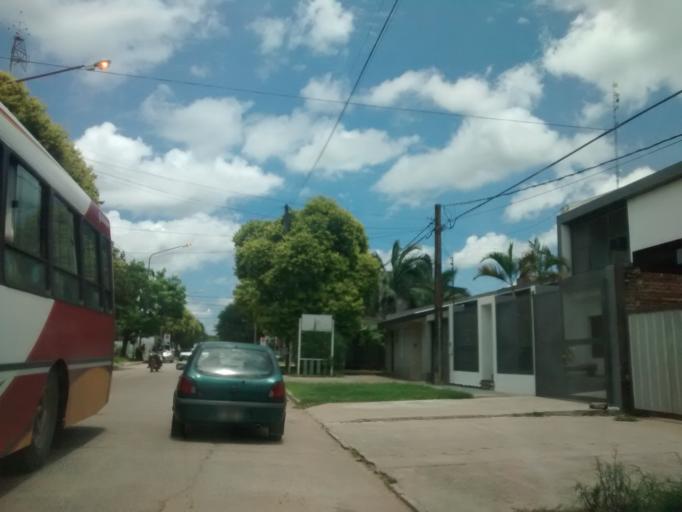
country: AR
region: Chaco
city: Fontana
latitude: -27.4348
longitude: -59.0022
